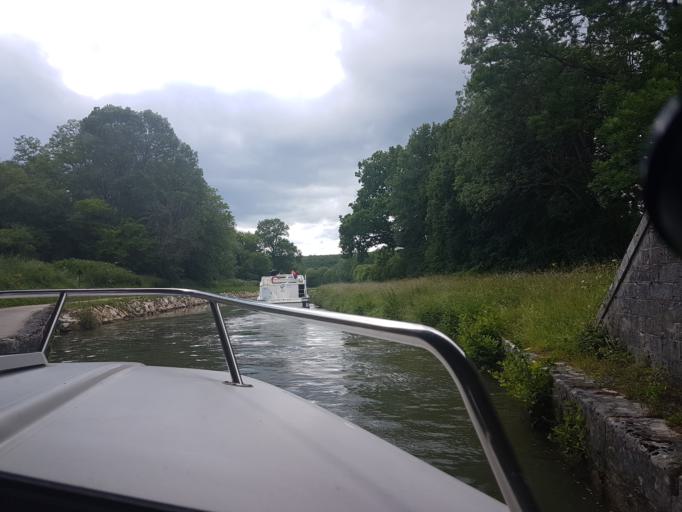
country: FR
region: Bourgogne
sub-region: Departement de l'Yonne
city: Vermenton
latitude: 47.5574
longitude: 3.6413
